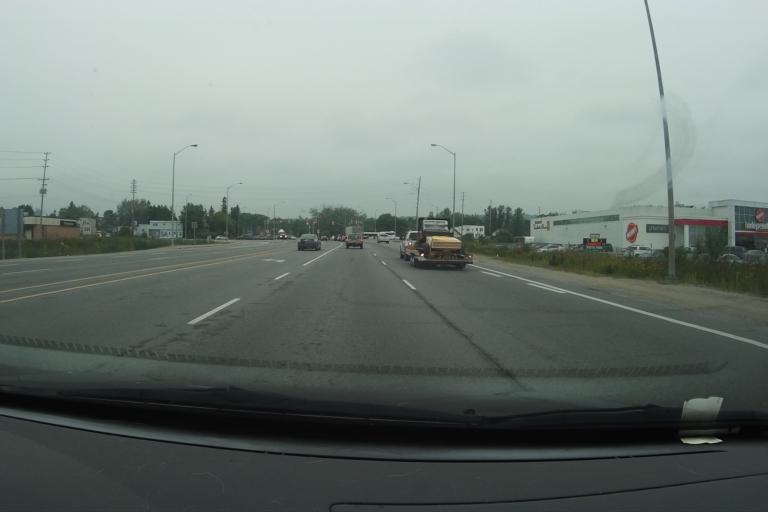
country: CA
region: Ontario
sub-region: Nipissing District
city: North Bay
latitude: 46.3164
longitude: -79.4433
